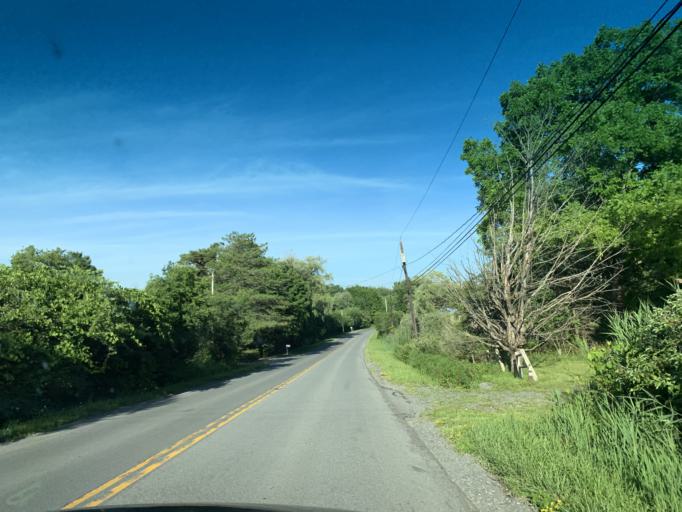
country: US
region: New York
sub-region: Oneida County
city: Clinton
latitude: 43.0553
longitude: -75.4347
